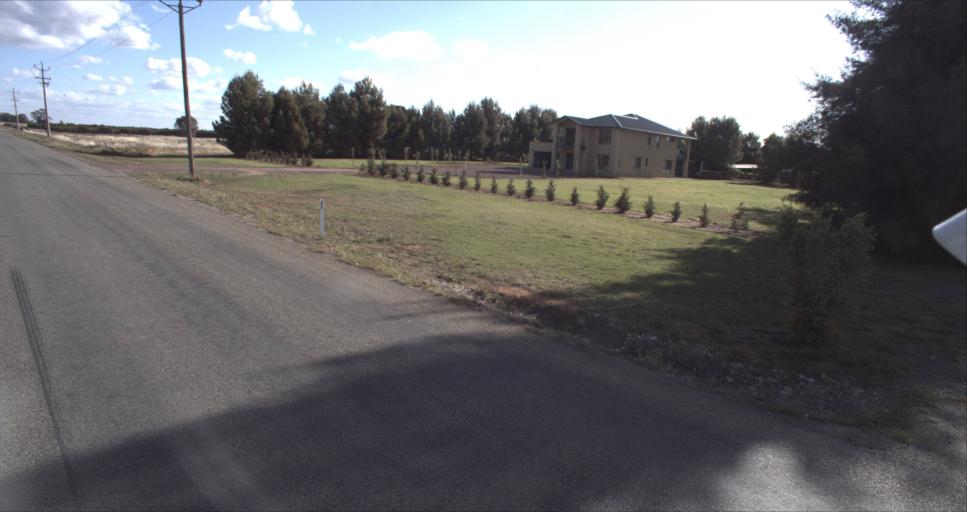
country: AU
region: New South Wales
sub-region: Leeton
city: Leeton
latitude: -34.5258
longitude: 146.2824
